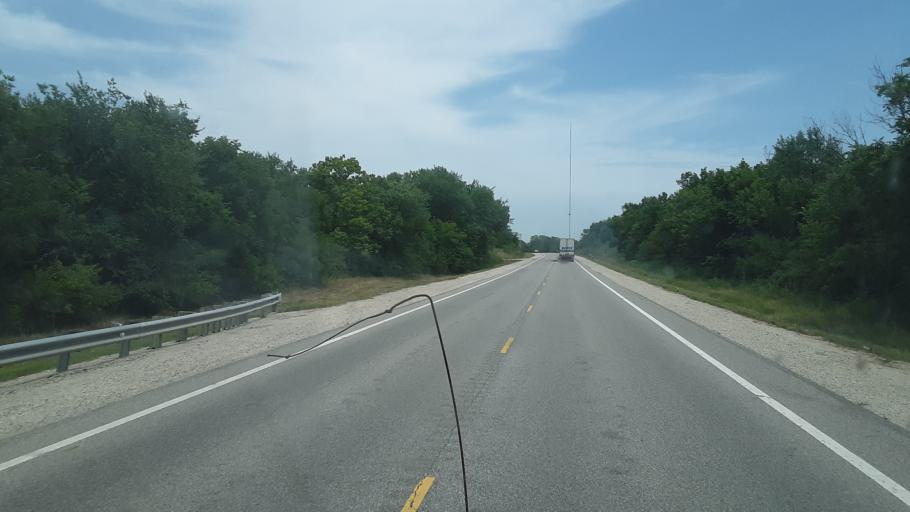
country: US
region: Kansas
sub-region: Allen County
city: Iola
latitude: 37.9125
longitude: -95.1329
